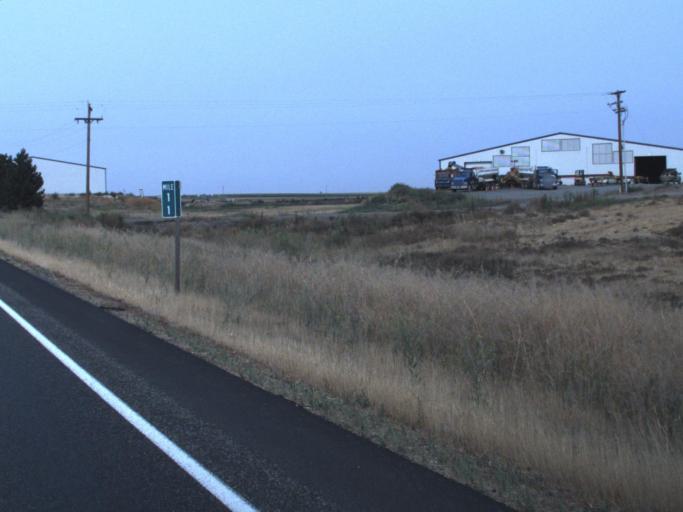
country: US
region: Washington
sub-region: Benton County
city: Prosser
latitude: 46.0945
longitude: -119.6019
